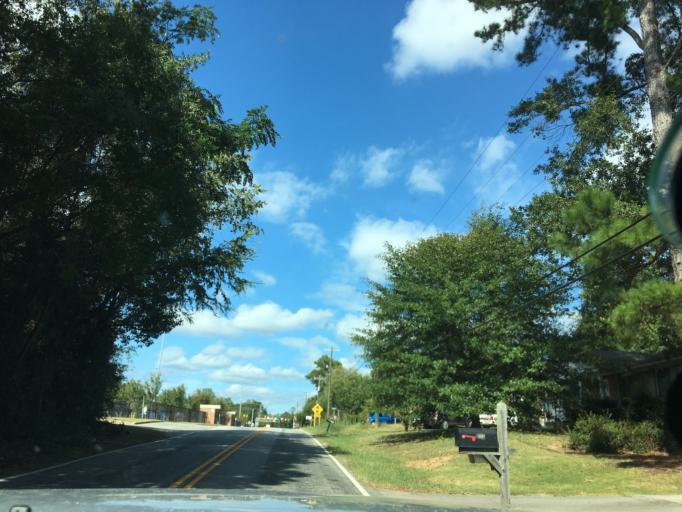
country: US
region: South Carolina
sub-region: Lexington County
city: Irmo
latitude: 34.0646
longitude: -81.1716
